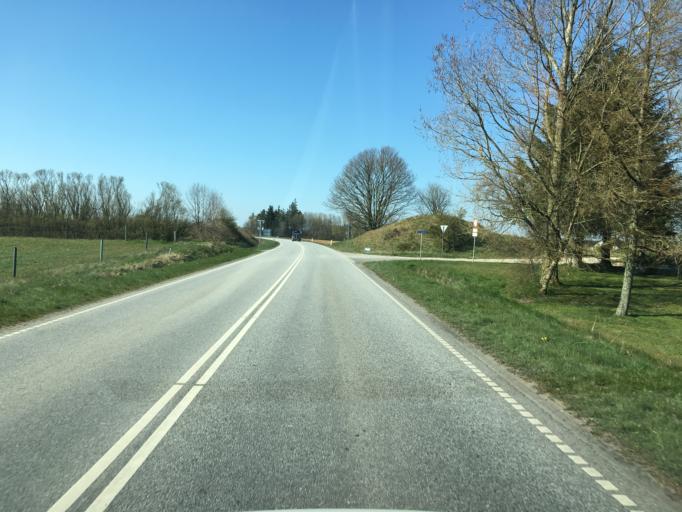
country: DK
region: South Denmark
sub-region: Aabenraa Kommune
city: Krusa
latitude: 54.9406
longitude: 9.3615
